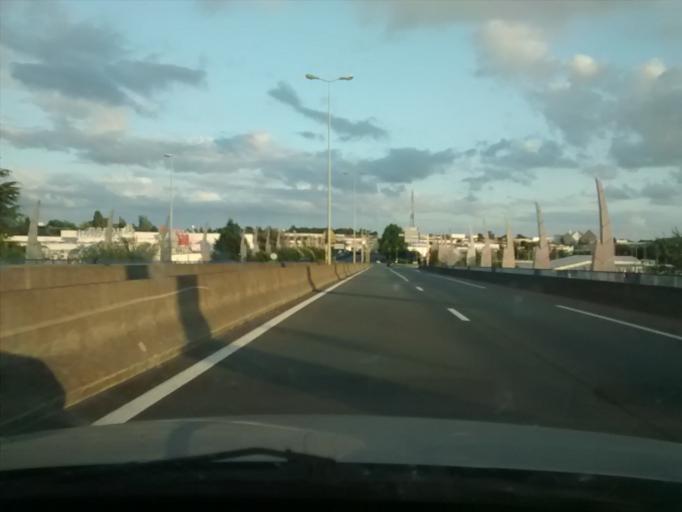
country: FR
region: Pays de la Loire
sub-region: Departement de la Sarthe
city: La Chapelle-Saint-Aubin
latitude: 48.0450
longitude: 0.1721
